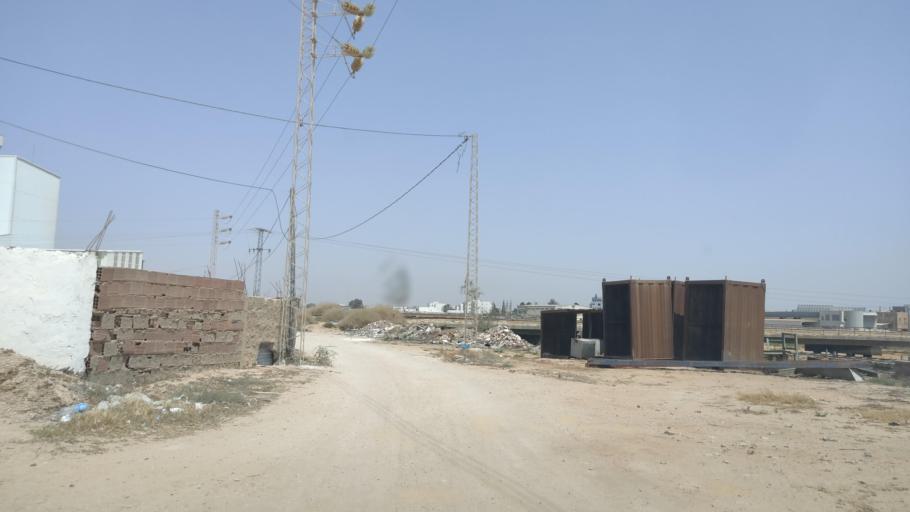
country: TN
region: Safaqis
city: Sfax
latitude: 34.7064
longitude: 10.7265
